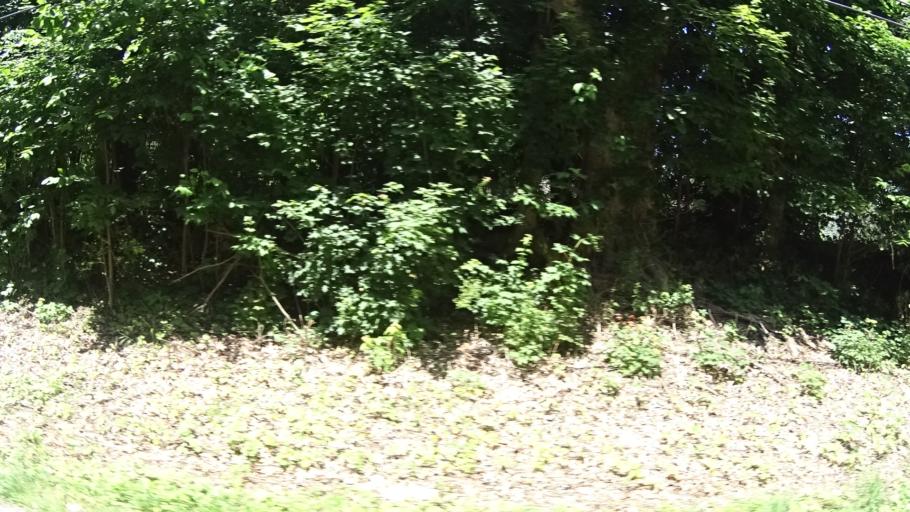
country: US
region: Ohio
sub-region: Lorain County
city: Vermilion
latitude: 41.3524
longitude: -82.3963
